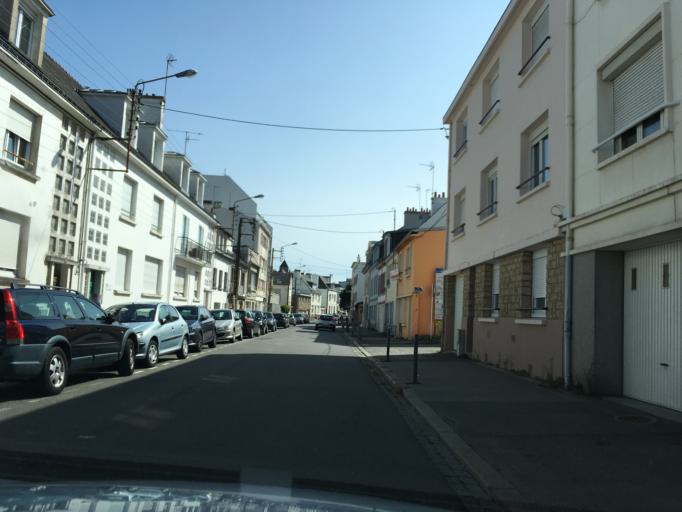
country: FR
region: Brittany
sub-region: Departement du Morbihan
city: Lorient
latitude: 47.7443
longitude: -3.3660
